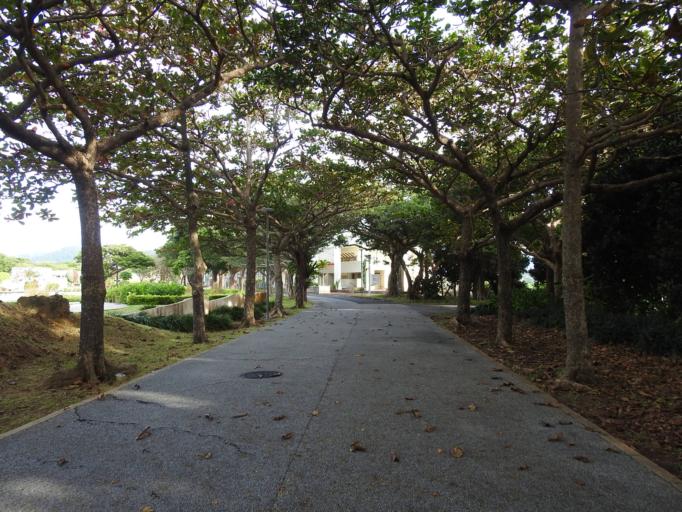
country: JP
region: Okinawa
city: Nago
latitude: 26.6809
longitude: 127.8818
